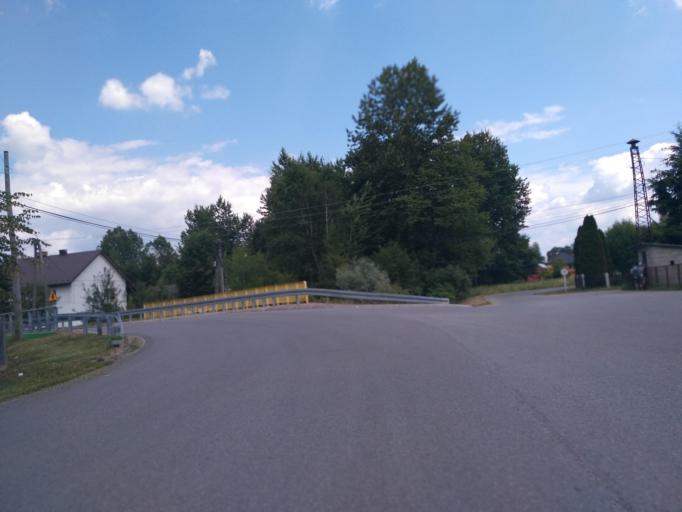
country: PL
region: Subcarpathian Voivodeship
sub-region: Powiat debicki
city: Brzostek
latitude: 49.8623
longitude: 21.4571
